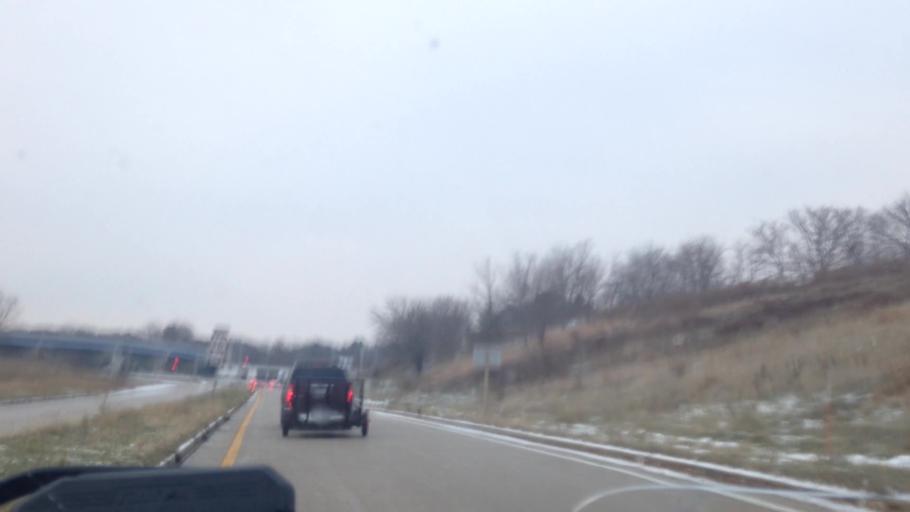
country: US
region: Wisconsin
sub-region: Waukesha County
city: Oconomowoc
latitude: 43.1092
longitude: -88.4813
